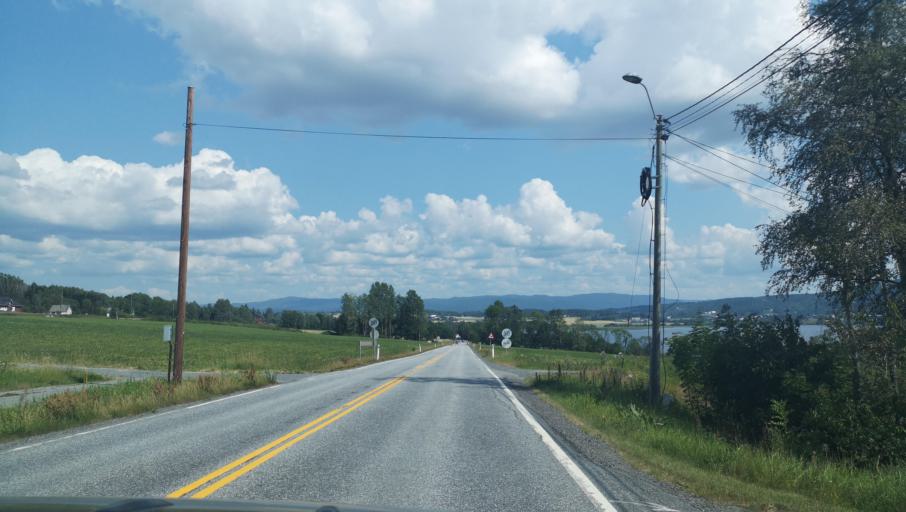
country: NO
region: Buskerud
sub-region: Ovre Eiker
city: Hokksund
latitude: 59.7041
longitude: 9.8071
